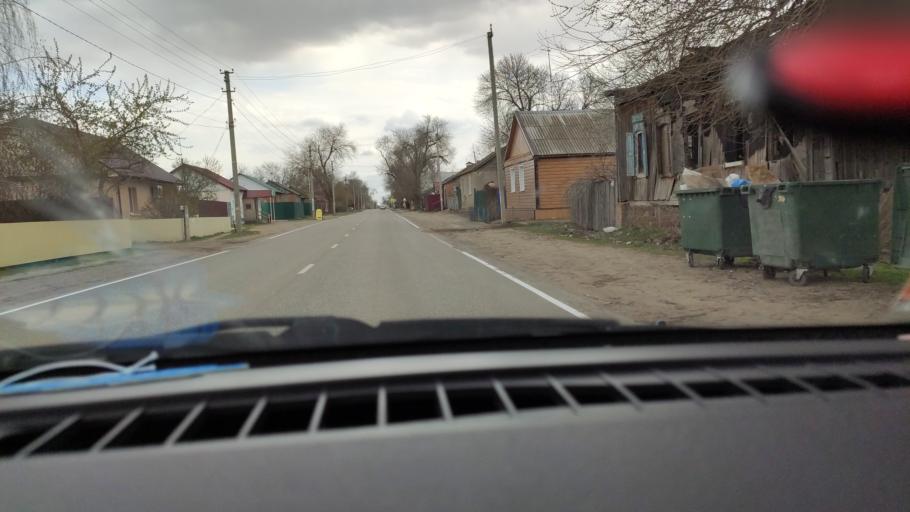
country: RU
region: Saratov
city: Privolzhskiy
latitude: 51.1847
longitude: 45.9179
